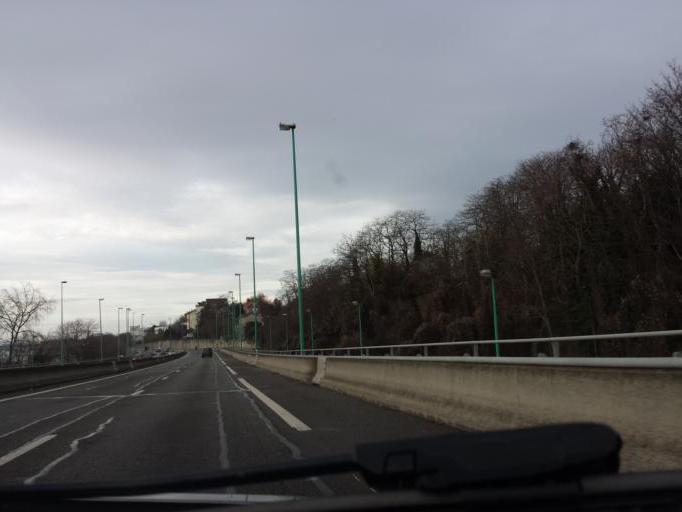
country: FR
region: Ile-de-France
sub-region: Departement du Val-d'Oise
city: Argenteuil
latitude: 48.9485
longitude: 2.2721
